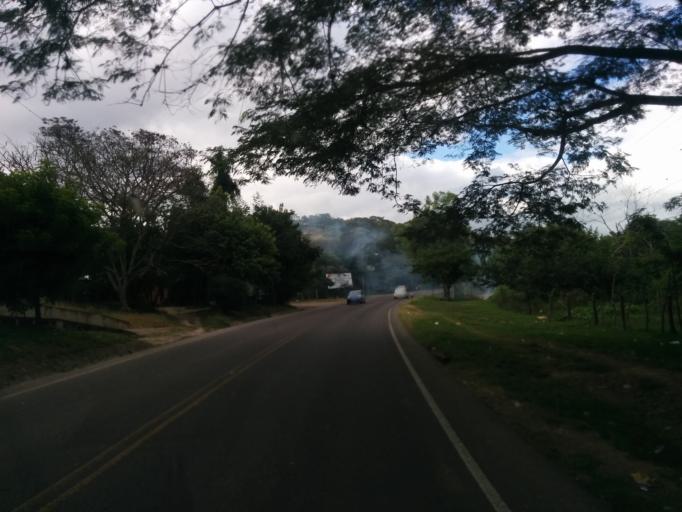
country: NI
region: Esteli
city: Esteli
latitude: 13.0031
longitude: -86.3077
